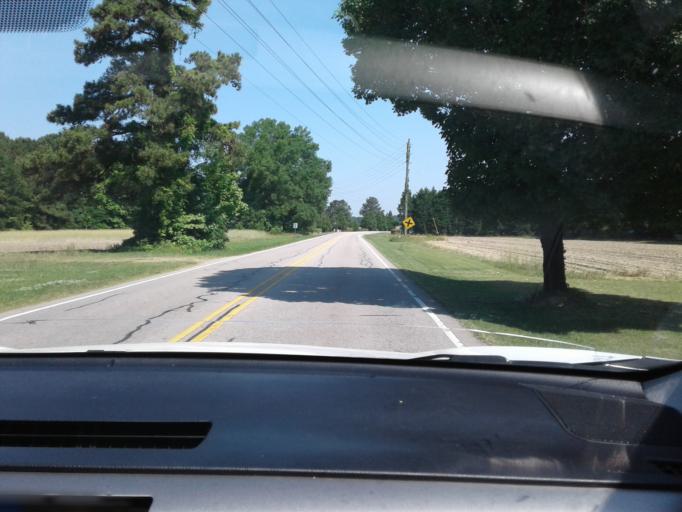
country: US
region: North Carolina
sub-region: Wake County
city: Fuquay-Varina
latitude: 35.6010
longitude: -78.8386
